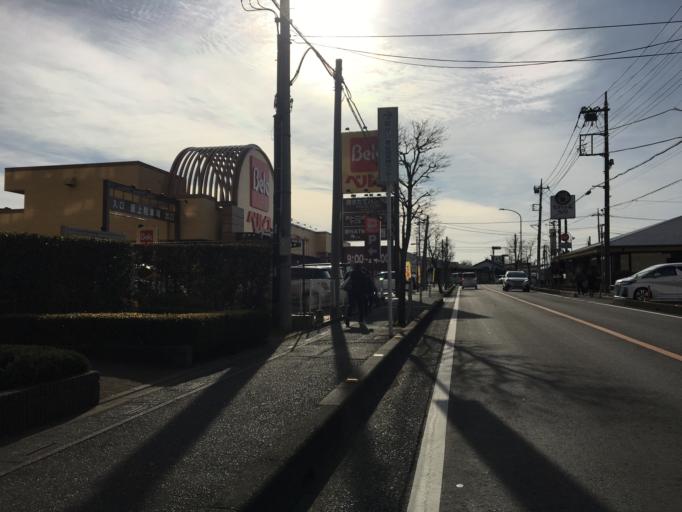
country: JP
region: Saitama
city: Oi
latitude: 35.8388
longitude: 139.5334
